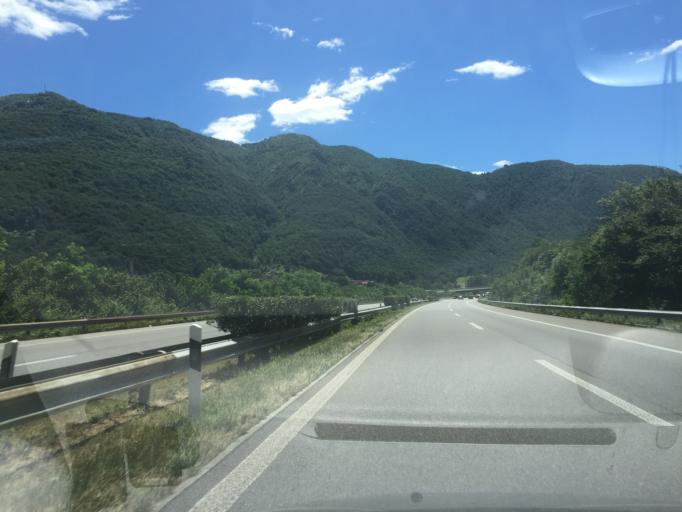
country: CH
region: Ticino
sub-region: Bellinzona District
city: Cadenazzo
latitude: 46.1122
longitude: 8.9293
